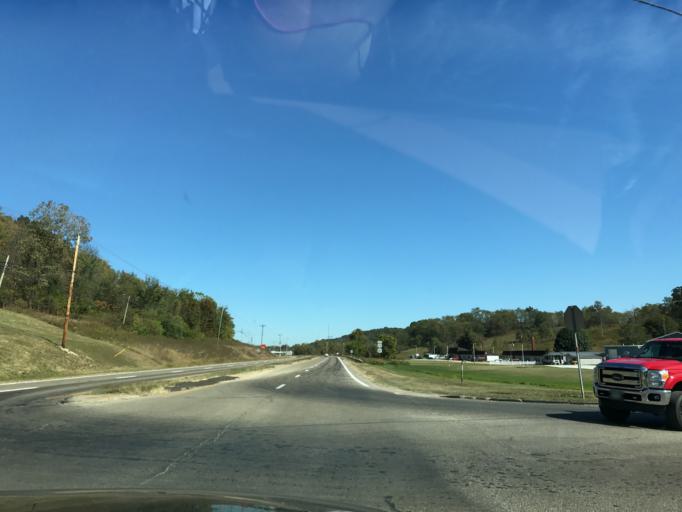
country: US
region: Ohio
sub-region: Muskingum County
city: New Concord
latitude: 40.0013
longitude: -81.6805
